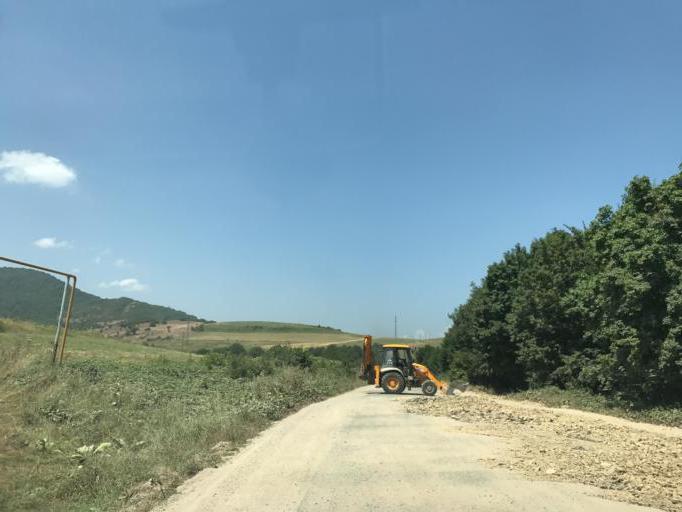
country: AZ
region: Tartar Rayon
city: Martakert
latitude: 40.1088
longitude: 46.6380
